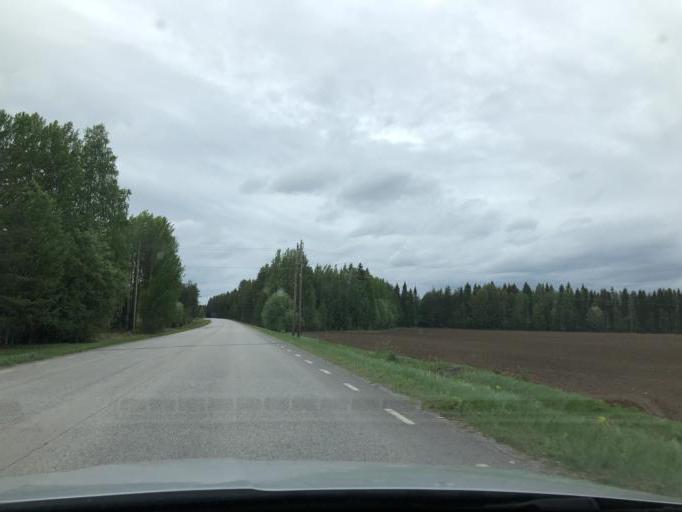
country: SE
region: Norrbotten
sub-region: Pitea Kommun
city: Bergsviken
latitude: 65.3592
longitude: 21.3763
